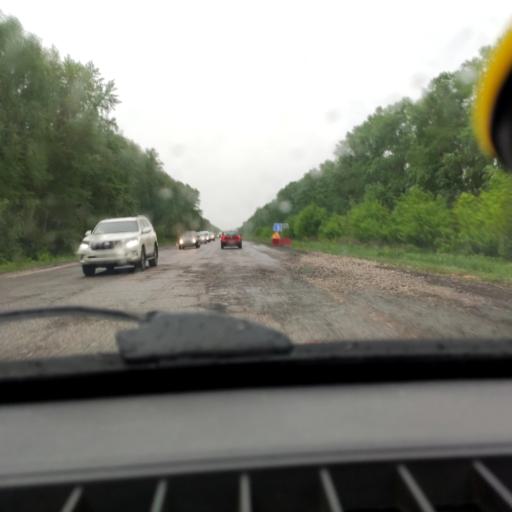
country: RU
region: Samara
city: Tol'yatti
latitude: 53.6499
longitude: 49.4227
